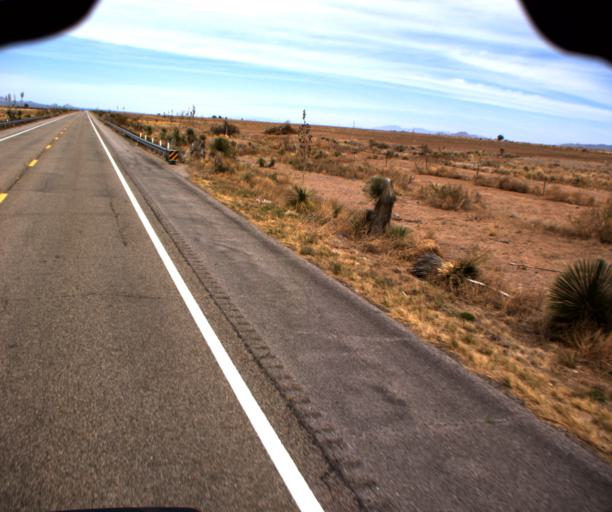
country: US
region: Arizona
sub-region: Cochise County
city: Pirtleville
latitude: 31.5404
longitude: -109.6567
